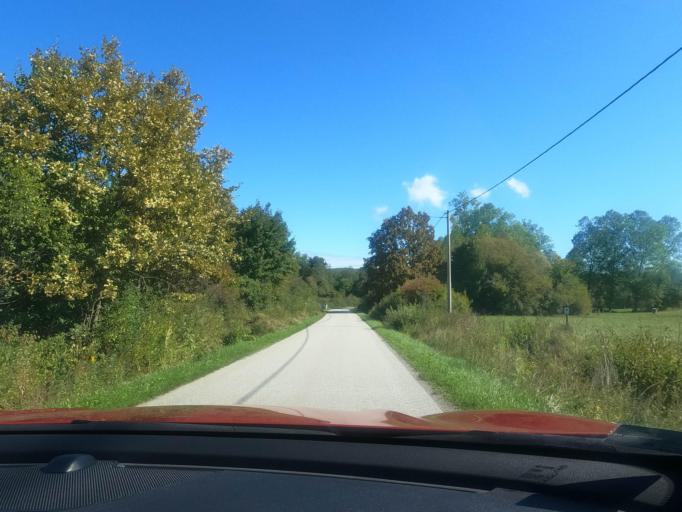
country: HR
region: Sisacko-Moslavacka
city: Petrinja
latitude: 45.3715
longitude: 16.2281
